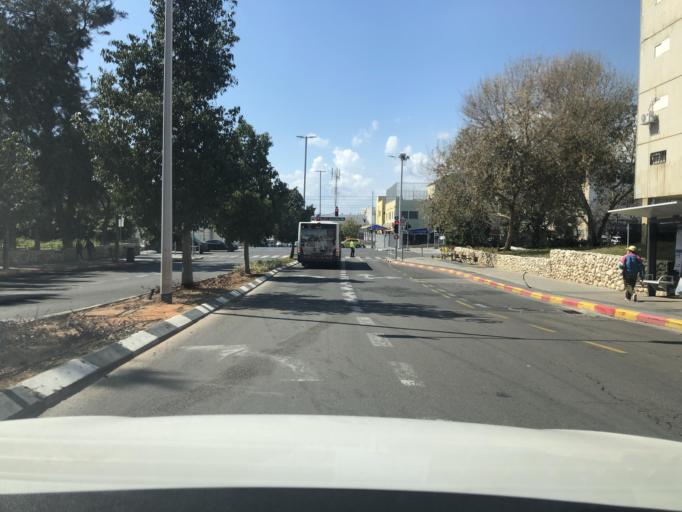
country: IL
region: Tel Aviv
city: Bat Yam
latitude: 32.0111
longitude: 34.7525
